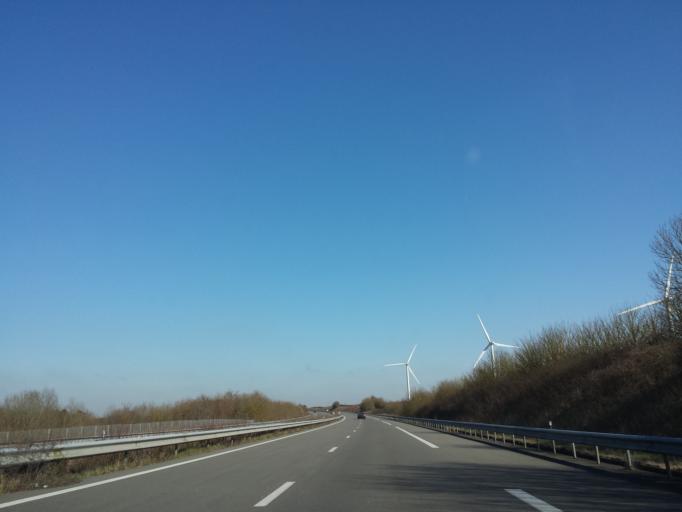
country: FR
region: Picardie
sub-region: Departement de l'Oise
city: Breteuil
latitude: 49.6911
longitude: 2.2289
